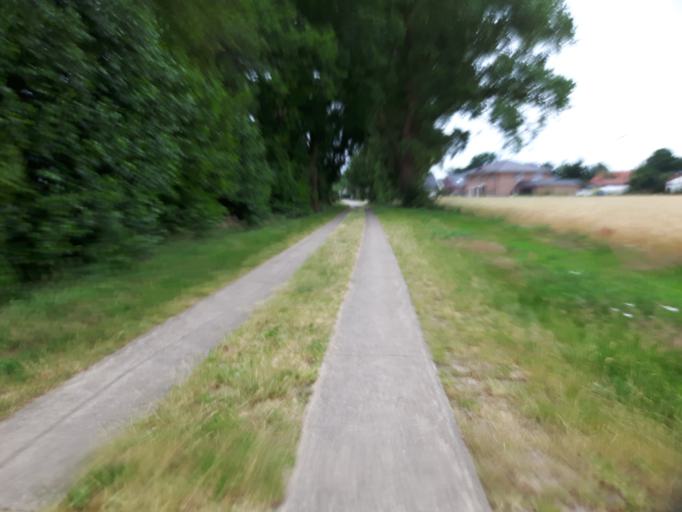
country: DE
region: Lower Saxony
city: Winsen
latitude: 53.3456
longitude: 10.1926
